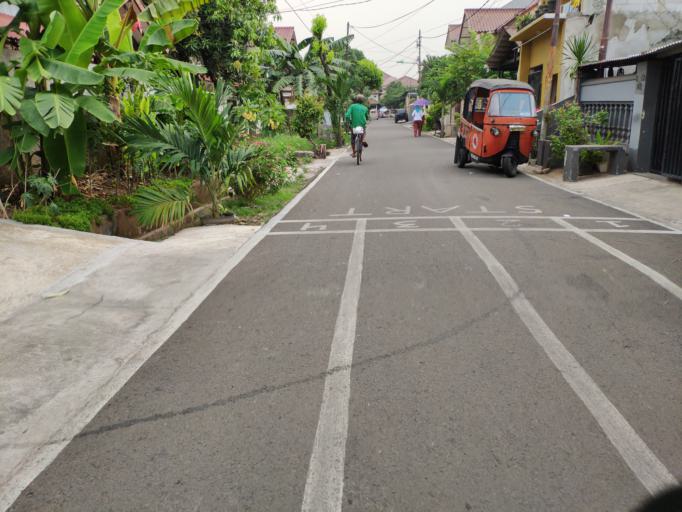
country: ID
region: Jakarta Raya
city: Jakarta
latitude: -6.1998
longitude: 106.8653
